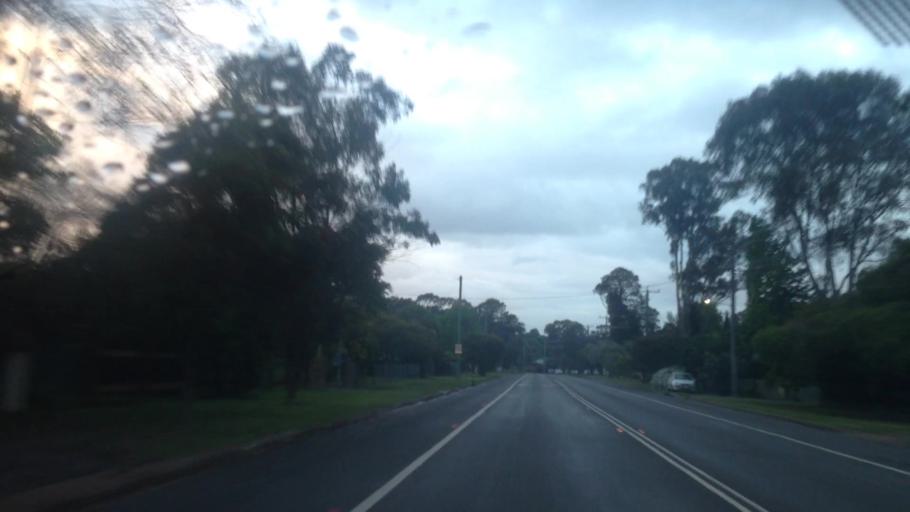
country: AU
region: New South Wales
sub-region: Lake Macquarie Shire
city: Cooranbong
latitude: -33.0828
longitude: 151.4476
